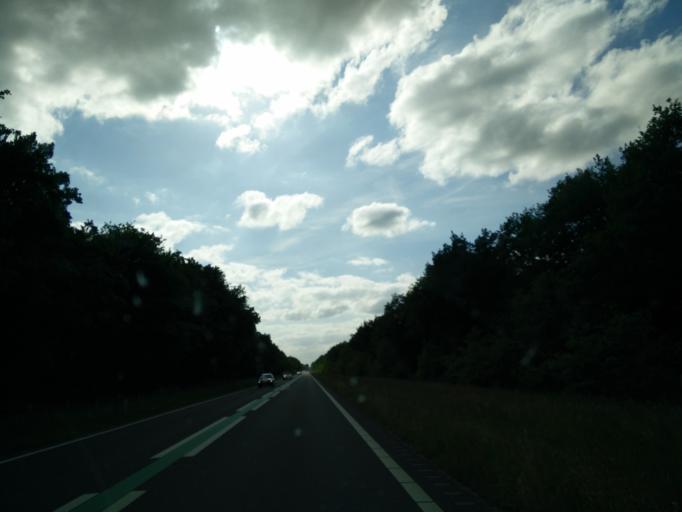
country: NL
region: Drenthe
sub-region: Gemeente Coevorden
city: Sleen
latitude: 52.7995
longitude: 6.7845
